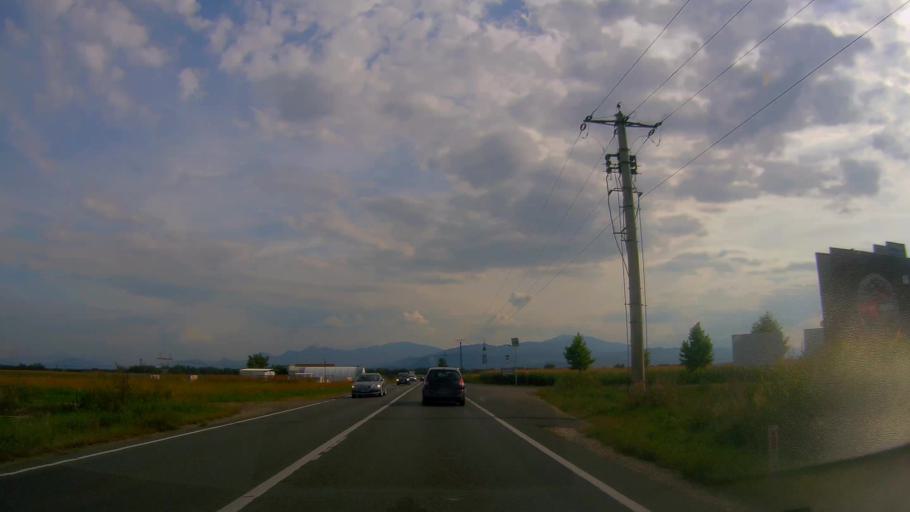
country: RO
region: Brasov
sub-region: Comuna Bod
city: Colonia Bod
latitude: 45.7227
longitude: 25.5789
